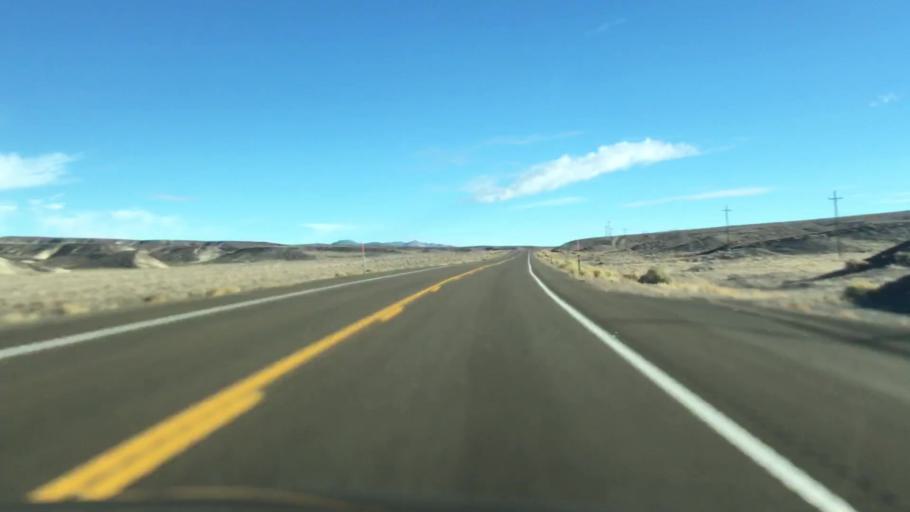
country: US
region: Nevada
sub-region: Mineral County
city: Hawthorne
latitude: 38.2340
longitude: -118.0240
